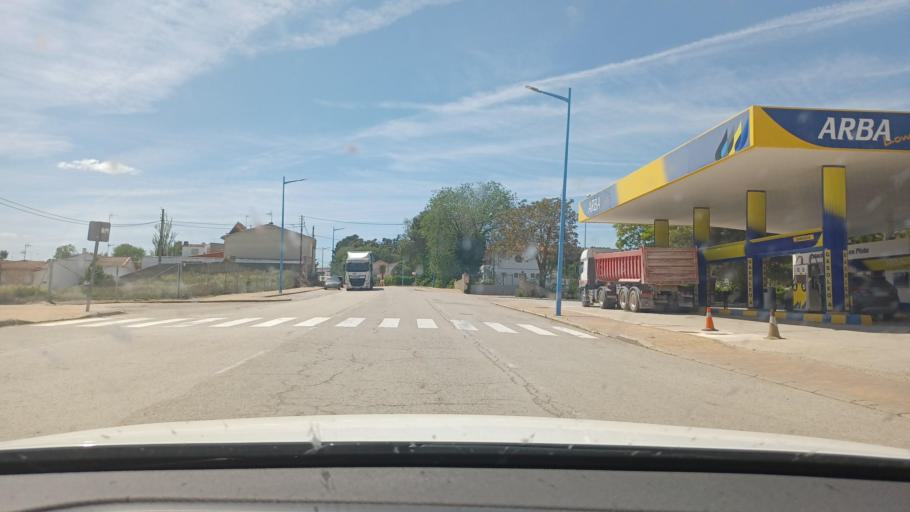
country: ES
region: Castille-La Mancha
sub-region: Provincia de Cuenca
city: Montalbo
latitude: 39.8816
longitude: -2.6681
